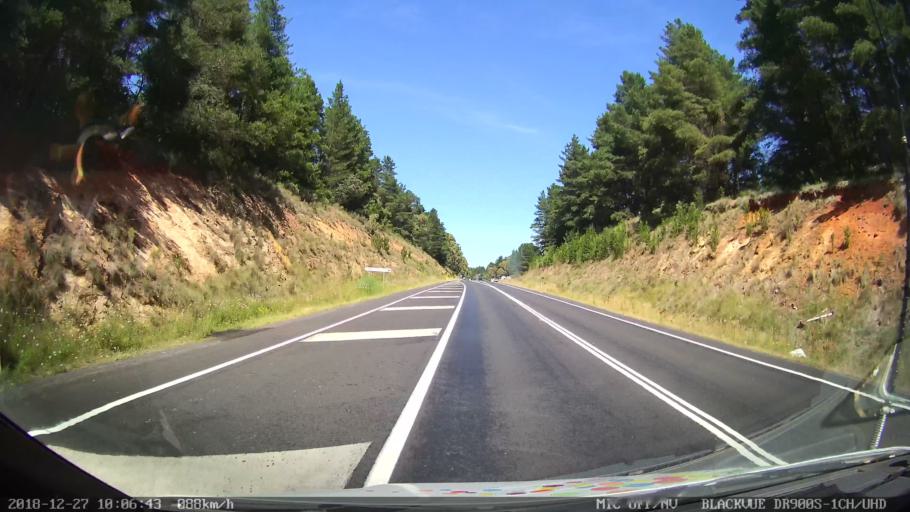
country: AU
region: New South Wales
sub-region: Lithgow
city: Portland
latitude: -33.4375
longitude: 149.8507
